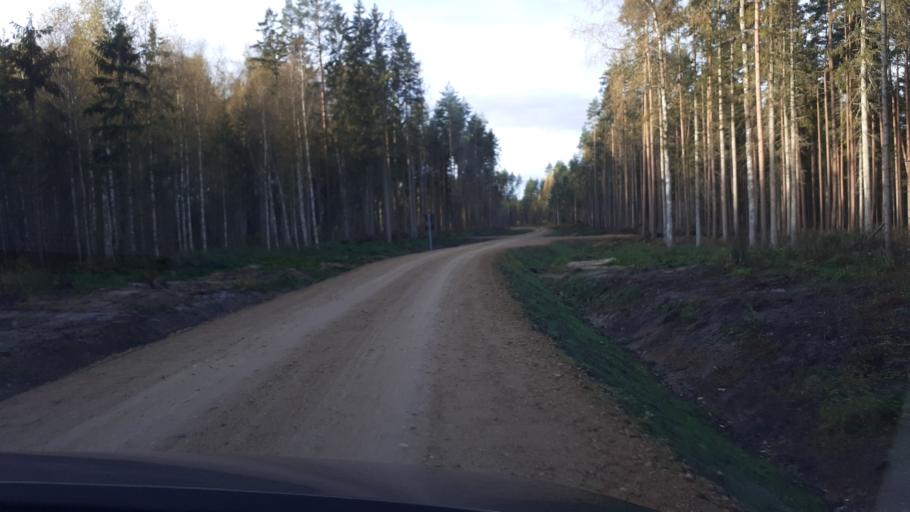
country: LV
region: Skrunda
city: Skrunda
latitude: 56.8501
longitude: 22.1063
